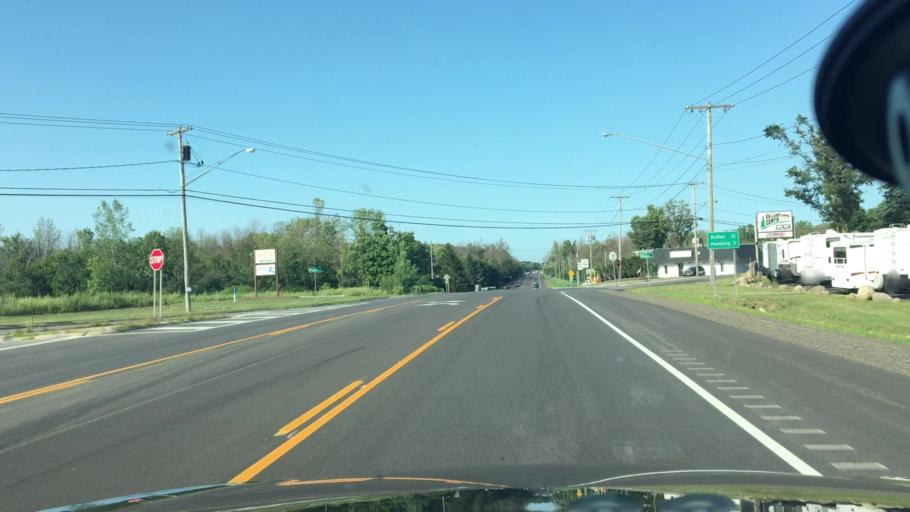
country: US
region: New York
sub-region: Erie County
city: Wanakah
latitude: 42.7269
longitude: -78.8906
